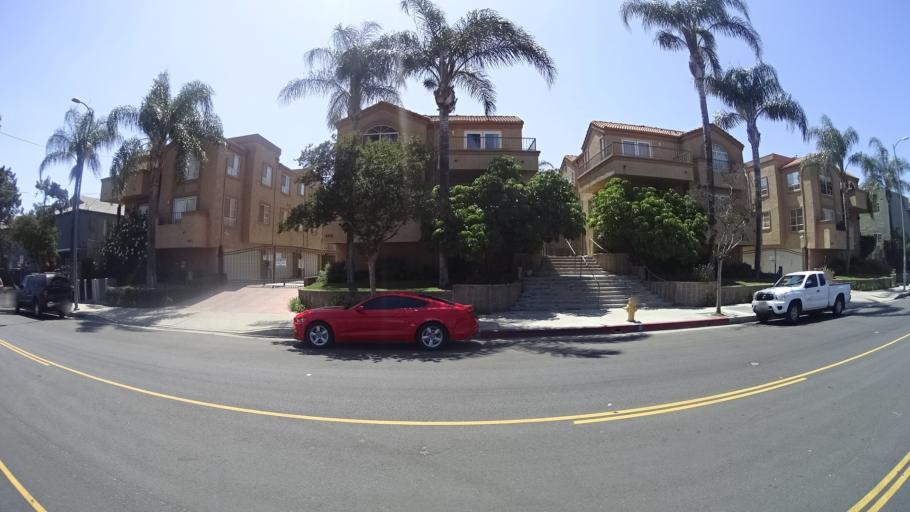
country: US
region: California
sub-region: Los Angeles County
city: Van Nuys
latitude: 34.1963
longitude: -118.4400
